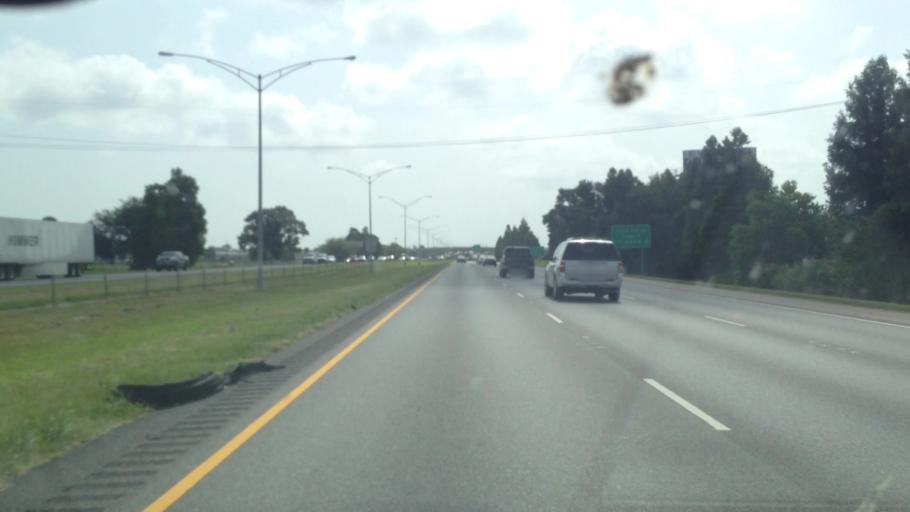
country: US
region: Louisiana
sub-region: Jefferson Parish
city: Kenner
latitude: 30.0086
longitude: -90.2523
